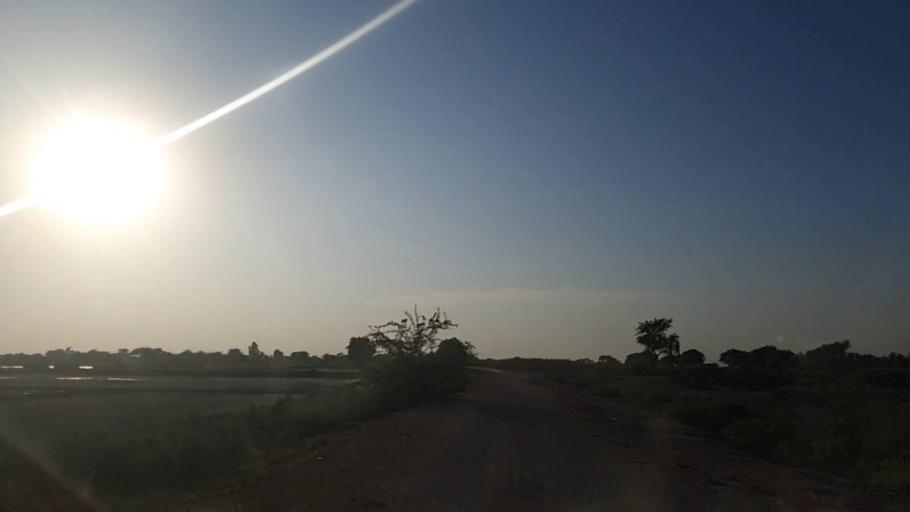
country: PK
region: Sindh
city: Jati
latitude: 24.4161
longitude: 68.1747
